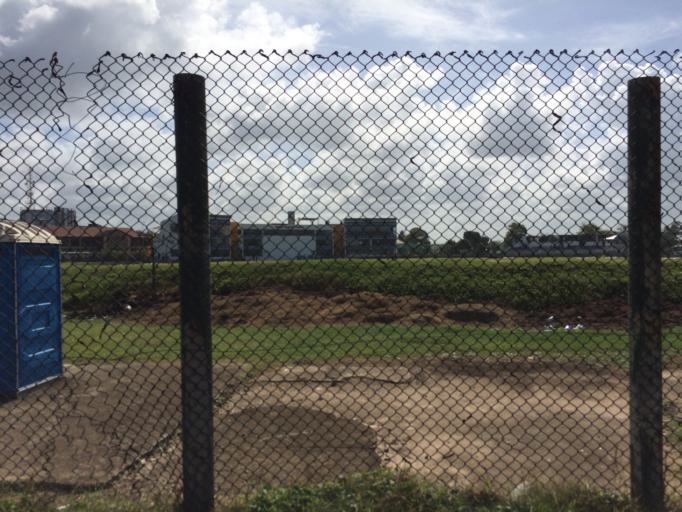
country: LK
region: Southern
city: Galle
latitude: 6.0311
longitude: 80.2150
